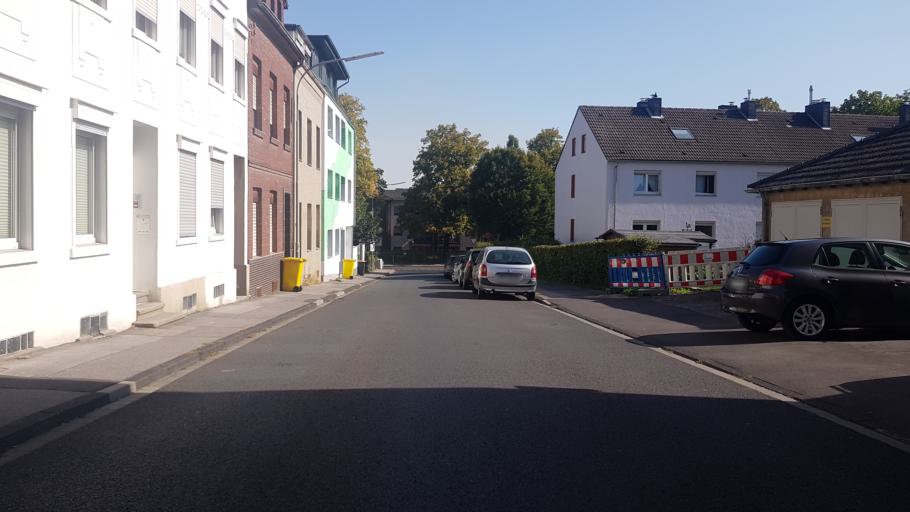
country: DE
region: North Rhine-Westphalia
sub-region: Regierungsbezirk Koln
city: Eschweiler
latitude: 50.8153
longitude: 6.2533
